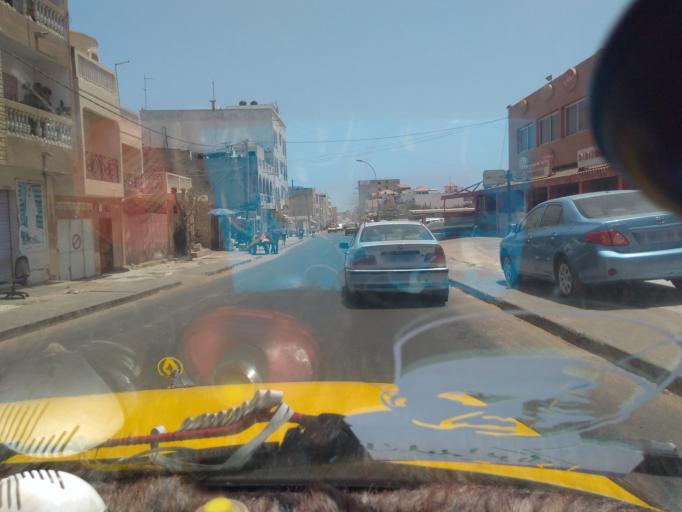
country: SN
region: Dakar
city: Grand Dakar
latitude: 14.7550
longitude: -17.4677
